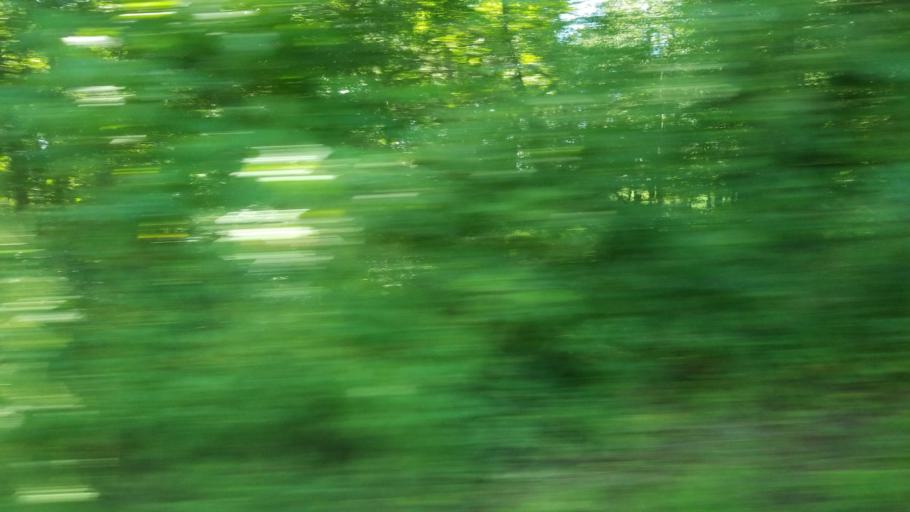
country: US
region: Illinois
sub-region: Williamson County
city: Johnston City
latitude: 37.7894
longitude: -88.8175
